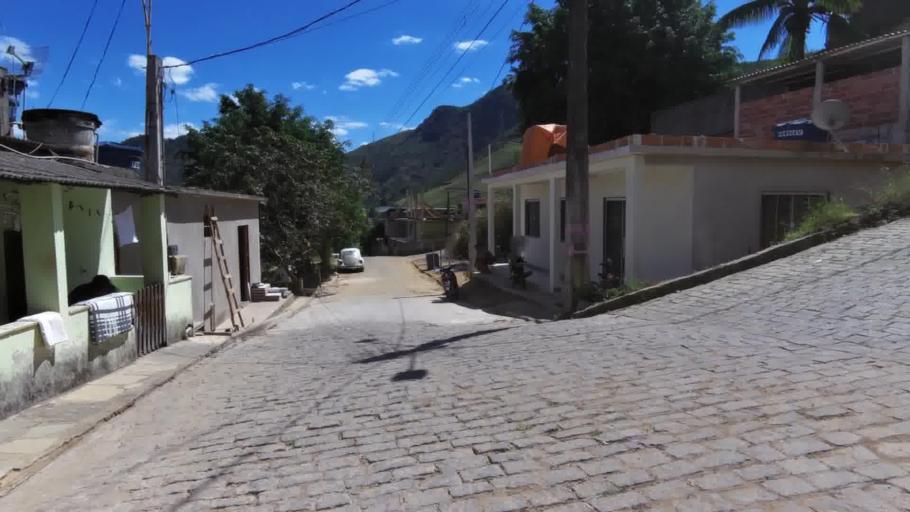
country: BR
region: Espirito Santo
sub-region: Rio Novo Do Sul
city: Rio Novo do Sul
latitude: -20.8659
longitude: -40.9429
